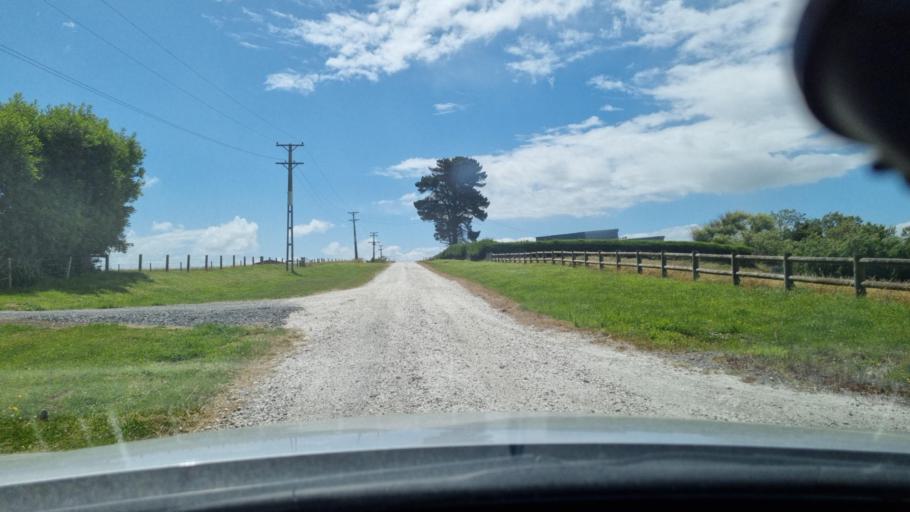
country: NZ
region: Southland
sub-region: Invercargill City
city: Invercargill
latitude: -46.4533
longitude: 168.3939
